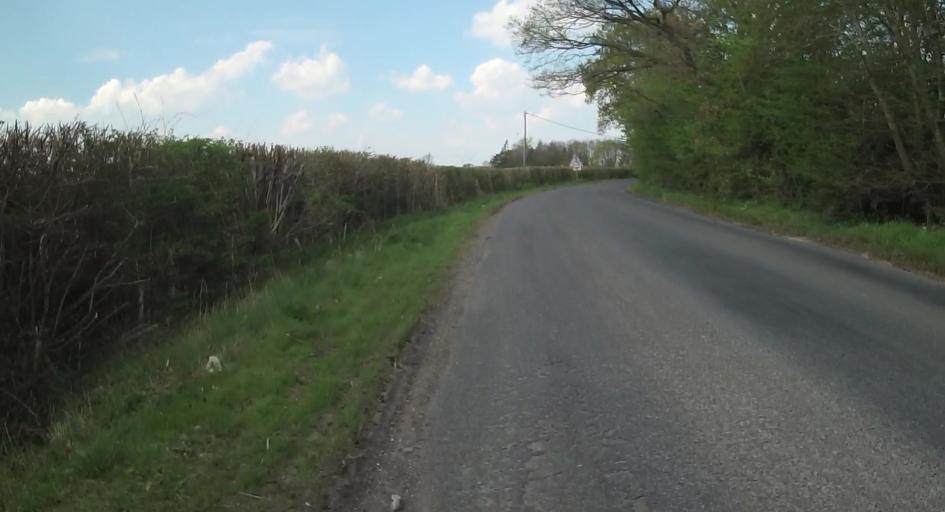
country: GB
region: England
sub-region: Hampshire
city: Tadley
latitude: 51.3233
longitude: -1.0774
